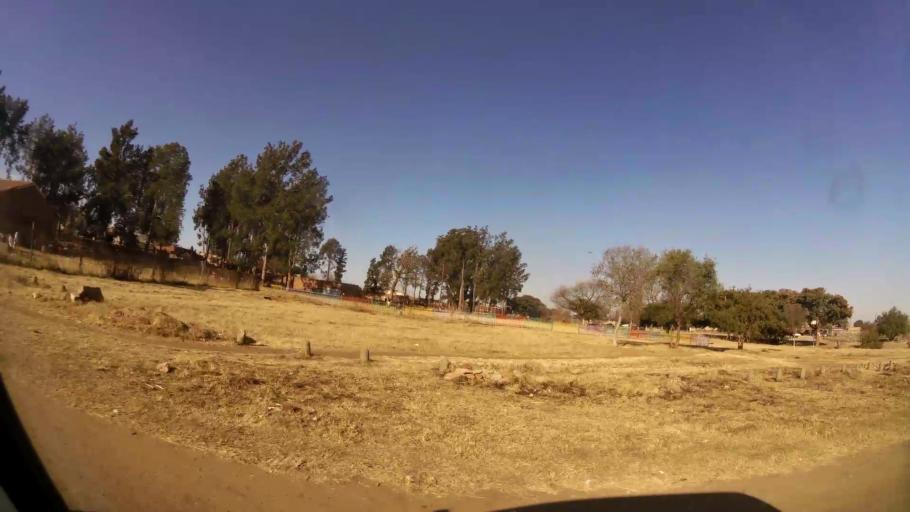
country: ZA
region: Gauteng
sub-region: City of Tshwane Metropolitan Municipality
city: Cullinan
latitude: -25.7075
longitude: 28.3722
